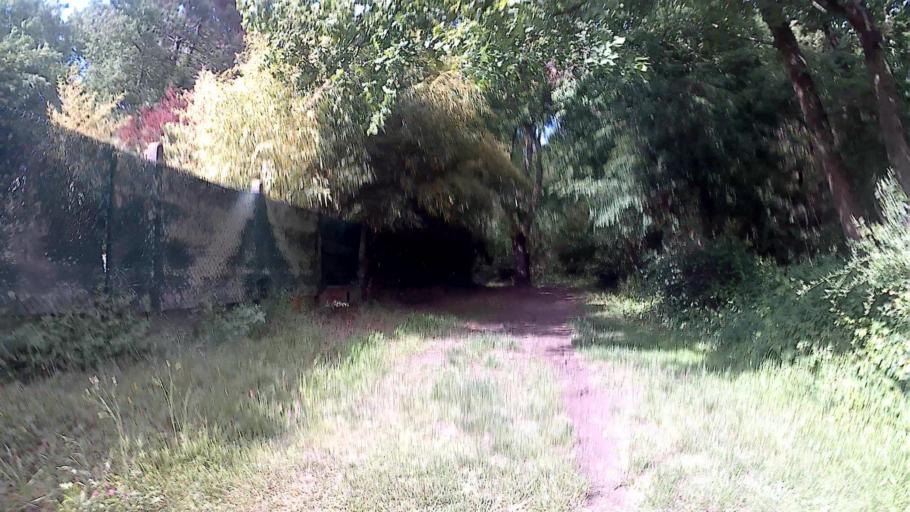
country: FR
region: Aquitaine
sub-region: Departement de la Gironde
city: Gradignan
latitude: 44.7823
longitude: -0.6183
